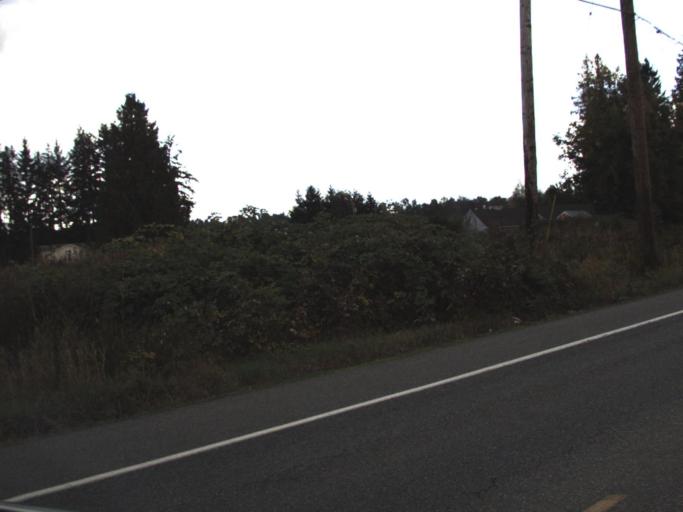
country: US
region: Washington
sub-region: Skagit County
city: Burlington
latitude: 48.4909
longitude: -122.2847
